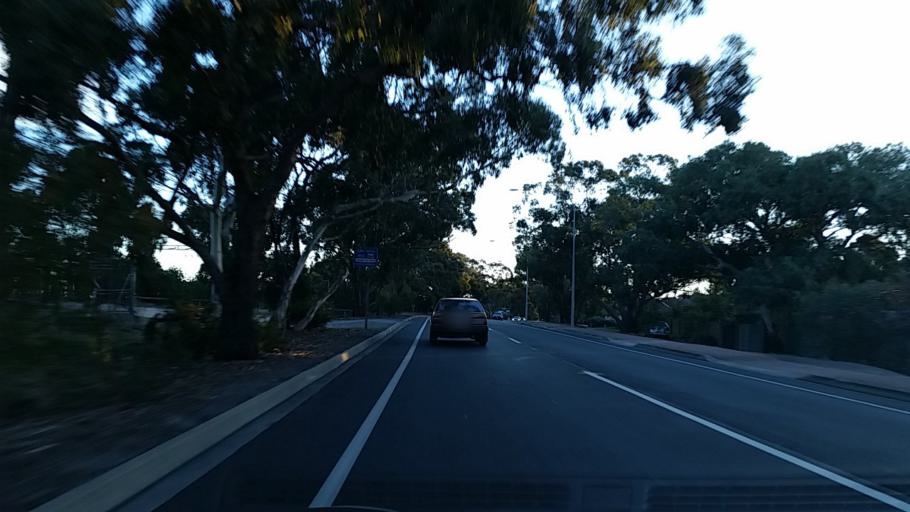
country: AU
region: South Australia
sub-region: Onkaparinga
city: Bedford Park
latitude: -35.0506
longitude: 138.5783
